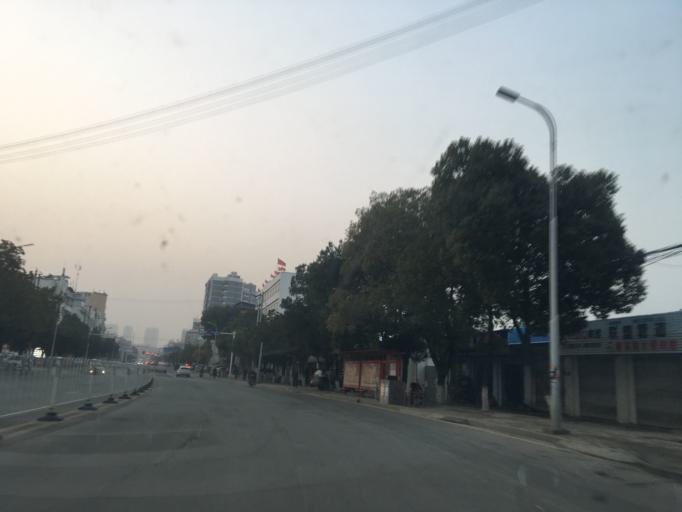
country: CN
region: Hubei
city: Macheng
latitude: 31.1716
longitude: 115.0257
